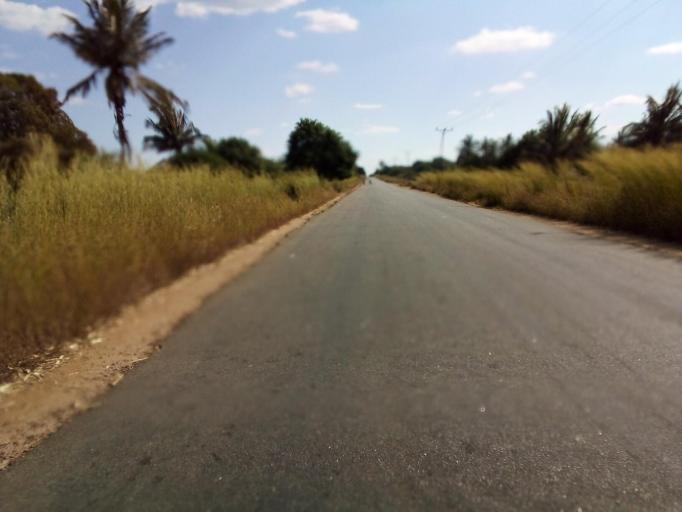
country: MZ
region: Zambezia
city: Quelimane
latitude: -17.5773
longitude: 36.6680
